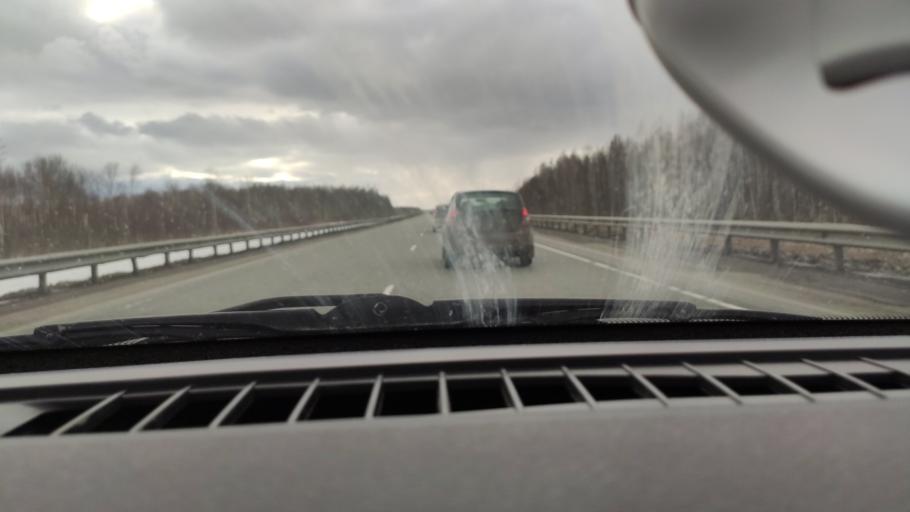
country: RU
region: Perm
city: Krasnokamsk
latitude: 58.1055
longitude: 55.7710
